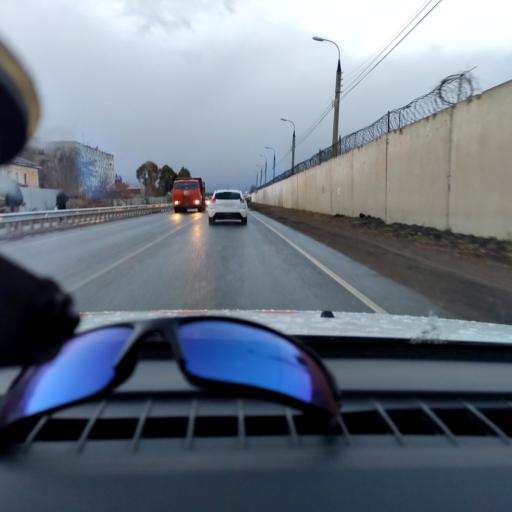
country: RU
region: Samara
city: Samara
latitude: 53.1333
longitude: 50.1063
